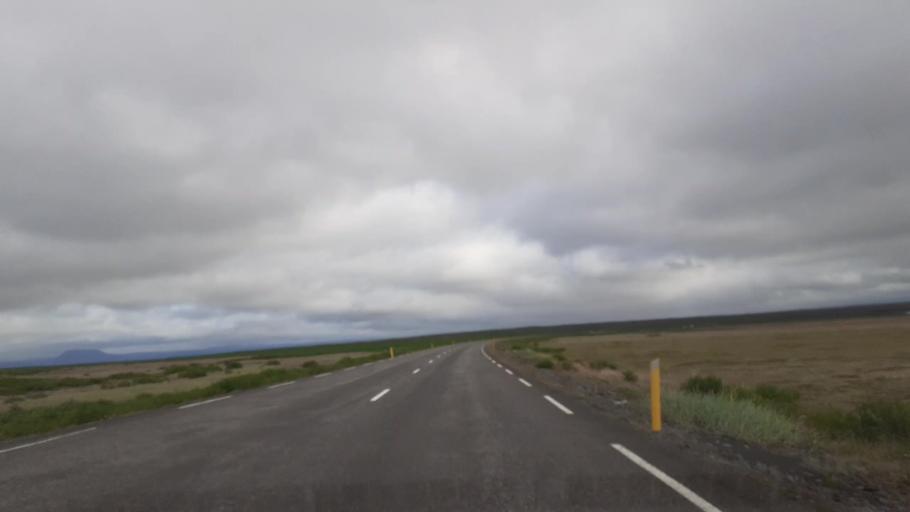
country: IS
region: Northeast
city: Husavik
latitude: 66.1172
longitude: -16.9148
